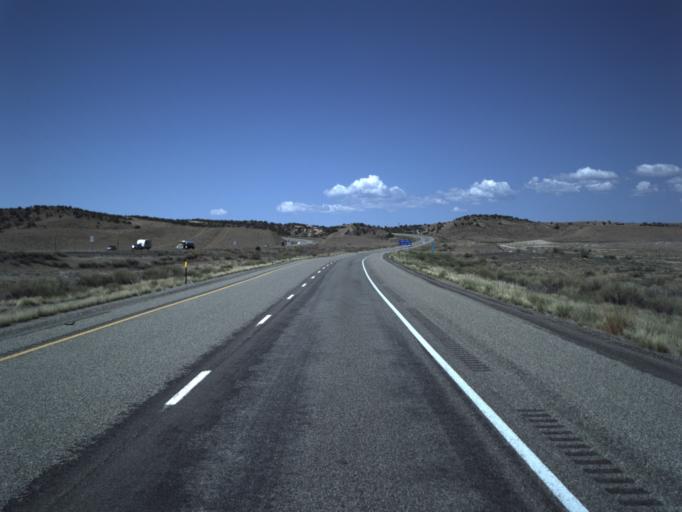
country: US
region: Colorado
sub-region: Mesa County
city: Loma
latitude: 39.1899
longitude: -109.0987
